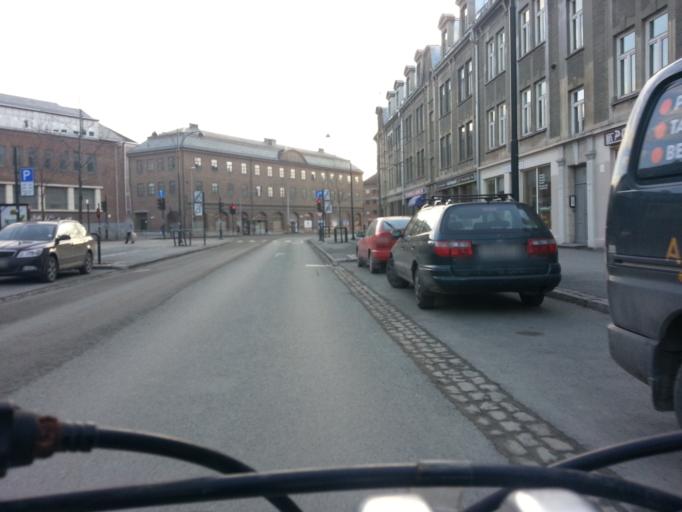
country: NO
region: Sor-Trondelag
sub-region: Trondheim
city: Trondheim
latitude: 63.4369
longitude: 10.4261
